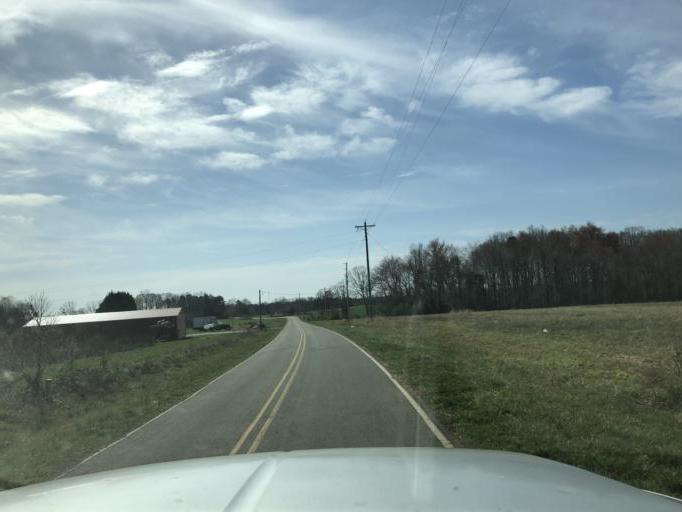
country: US
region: North Carolina
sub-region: Cleveland County
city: Shelby
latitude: 35.4780
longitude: -81.6417
